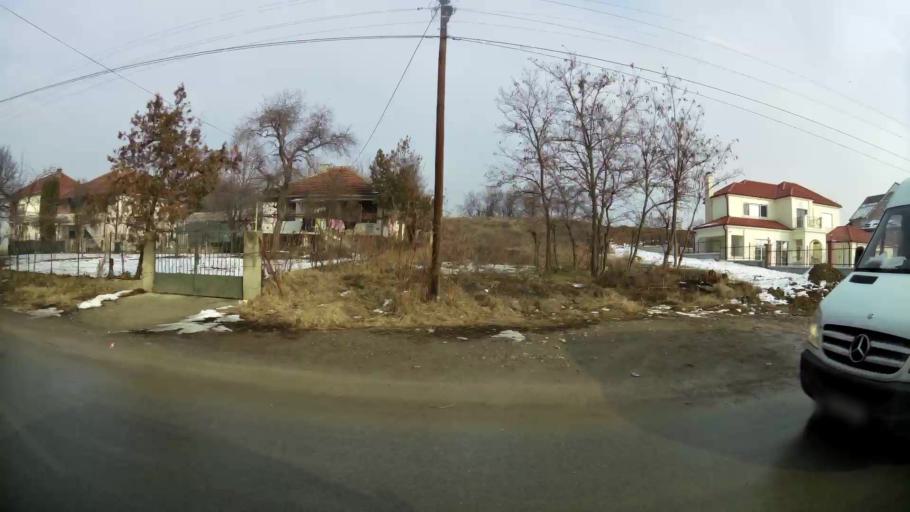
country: MK
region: Ilinden
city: Marino
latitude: 41.9915
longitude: 21.5900
